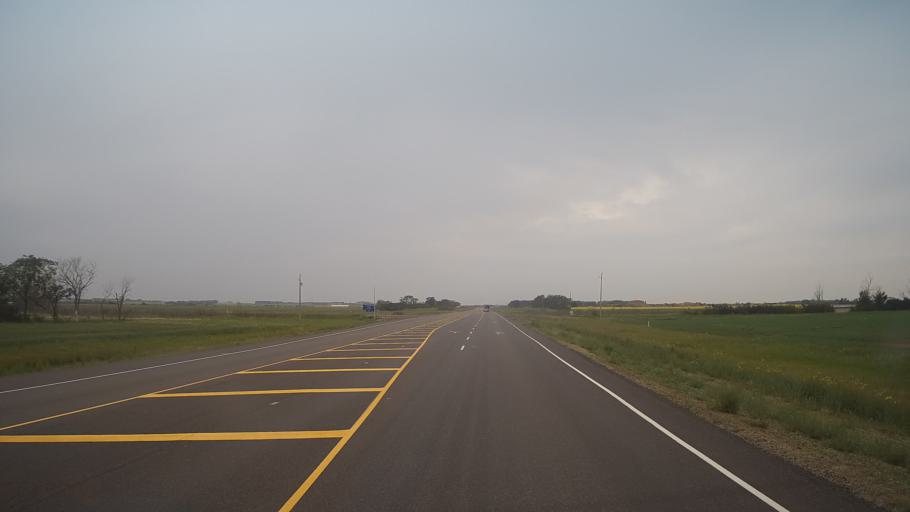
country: CA
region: Saskatchewan
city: Dalmeny
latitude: 52.1293
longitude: -106.8572
